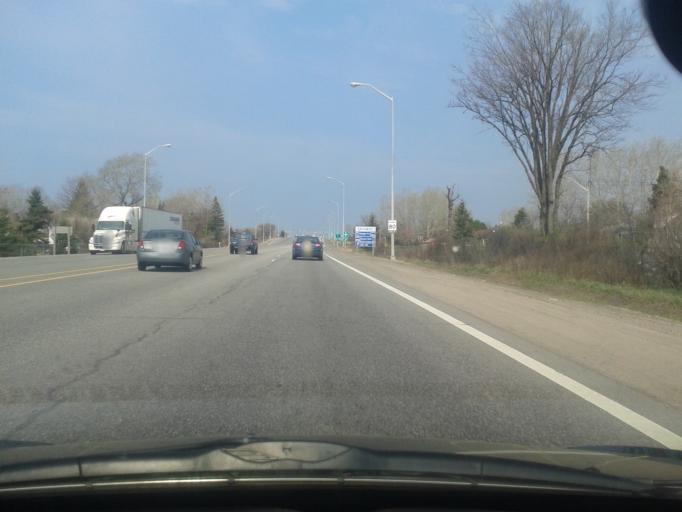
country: CA
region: Ontario
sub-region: Nipissing District
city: North Bay
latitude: 46.3284
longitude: -79.4588
